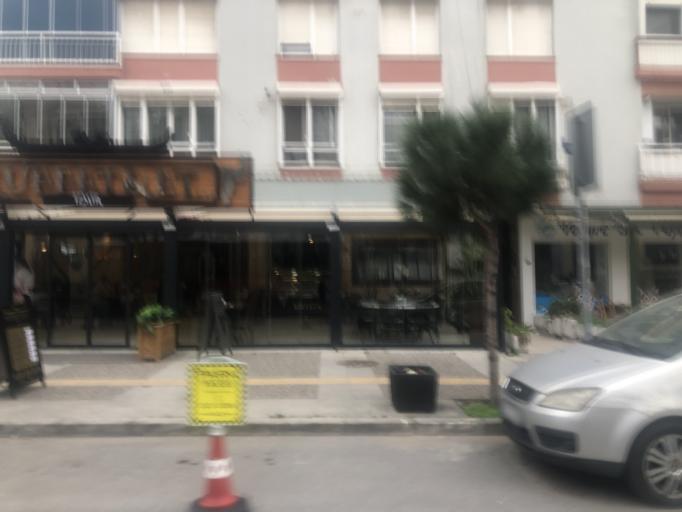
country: TR
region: Izmir
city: Karsiyaka
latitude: 38.4531
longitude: 27.1055
